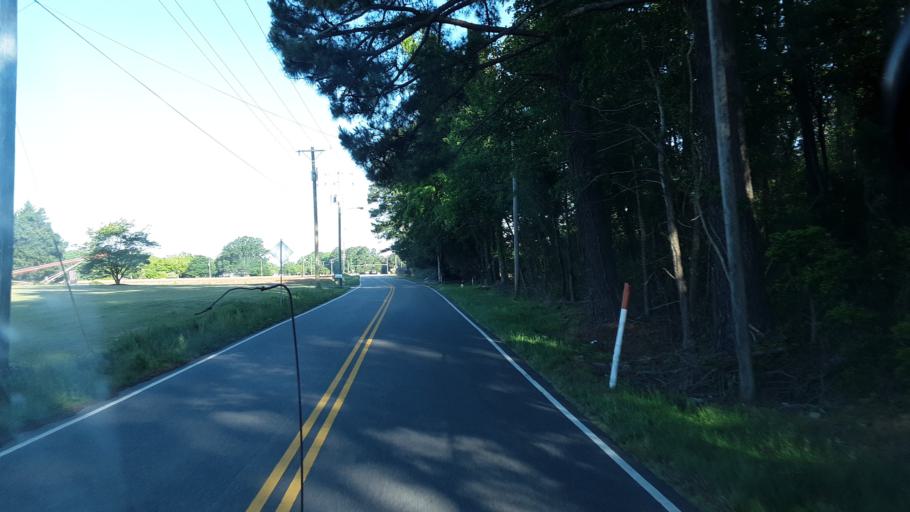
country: US
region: Virginia
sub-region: City of Virginia Beach
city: Virginia Beach
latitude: 36.7206
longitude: -76.0463
